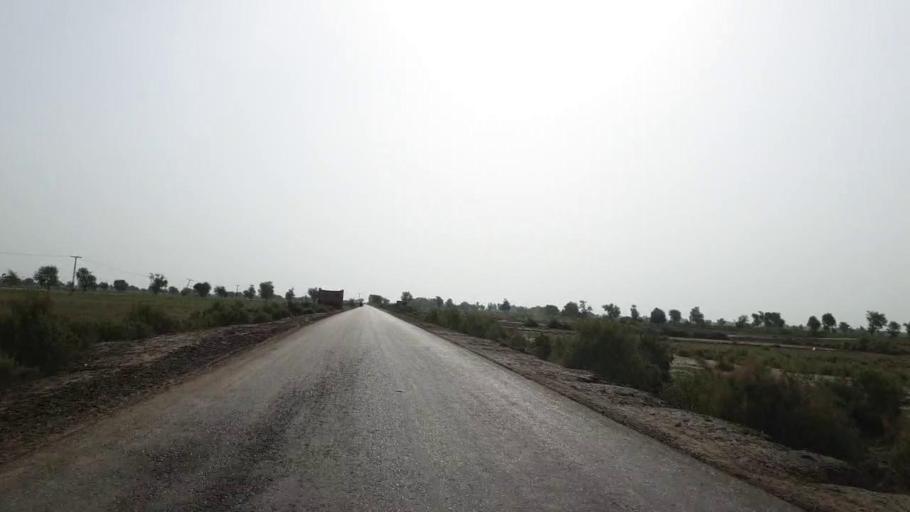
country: PK
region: Sindh
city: Jam Sahib
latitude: 26.2836
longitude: 68.5868
